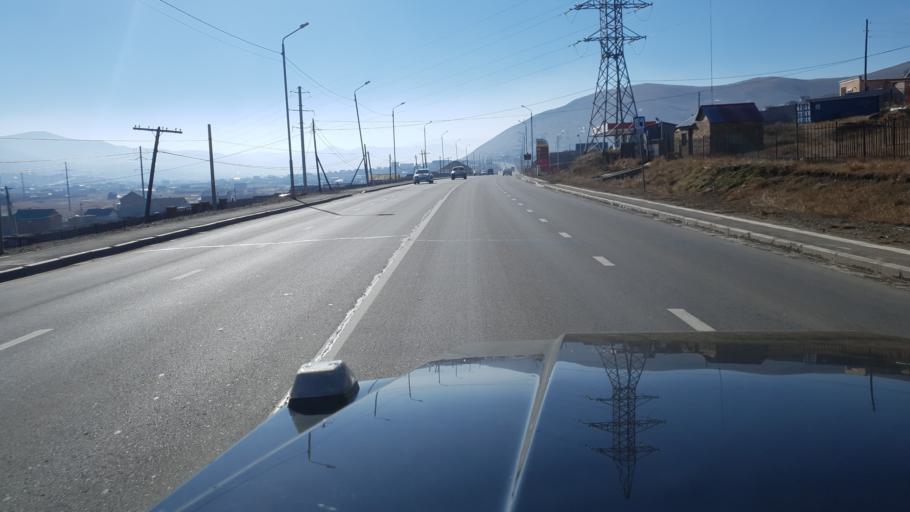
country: MN
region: Ulaanbaatar
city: Ulaanbaatar
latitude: 48.0245
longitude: 106.9136
